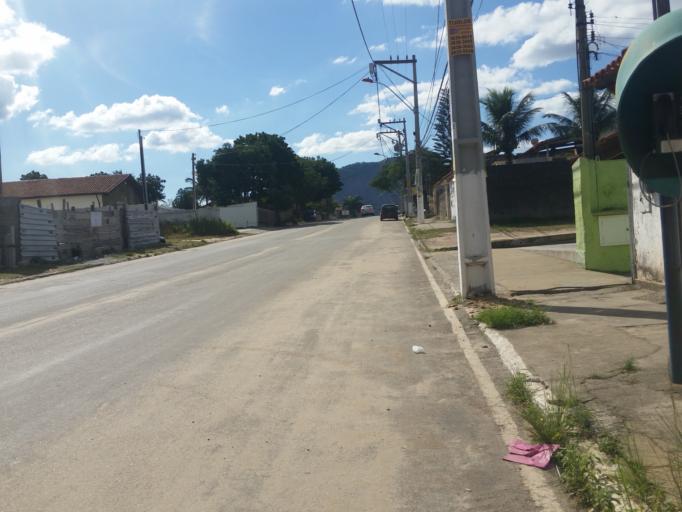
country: BR
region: Rio de Janeiro
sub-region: Marica
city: Marica
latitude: -22.9668
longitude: -42.9621
